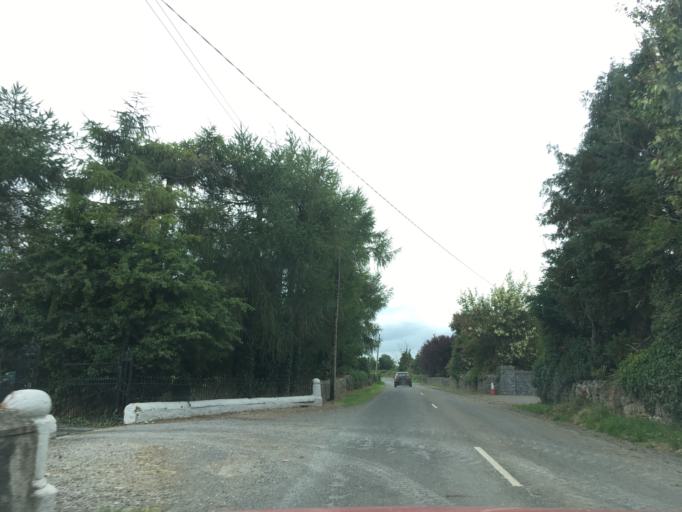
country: IE
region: Munster
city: Cahir
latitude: 52.4583
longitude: -7.9781
